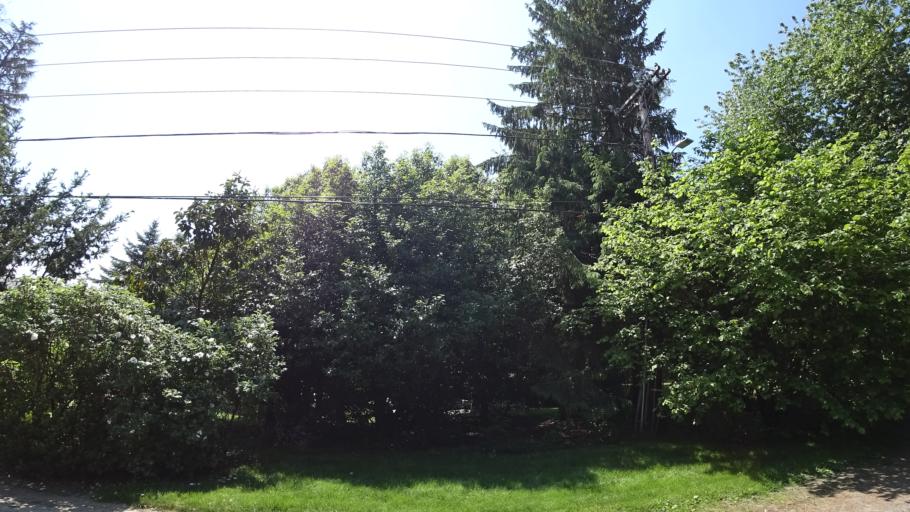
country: US
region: Oregon
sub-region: Clackamas County
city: Lake Oswego
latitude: 45.4355
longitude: -122.7123
